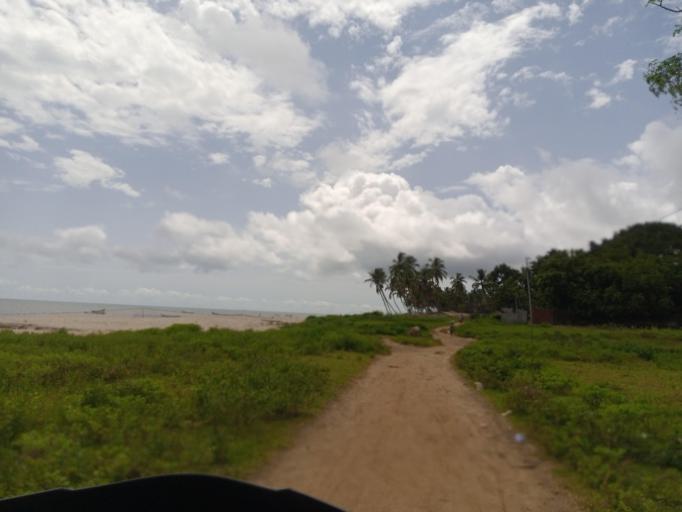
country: SL
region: Northern Province
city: Tintafor
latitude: 8.6202
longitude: -13.2137
